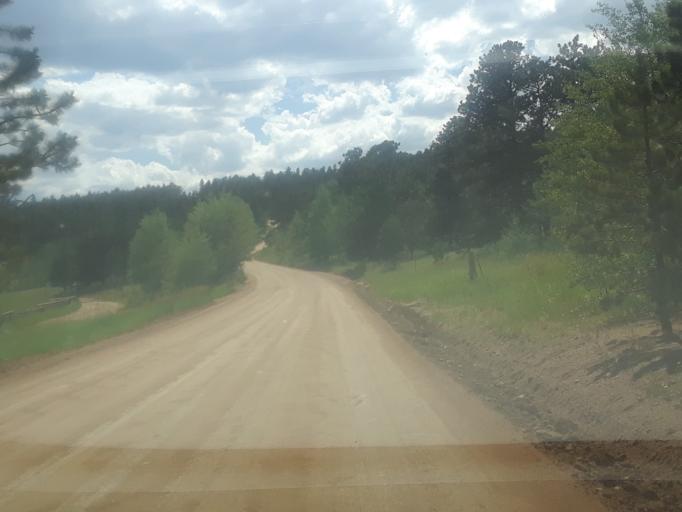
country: US
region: Colorado
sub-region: Boulder County
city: Nederland
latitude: 40.0486
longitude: -105.4893
